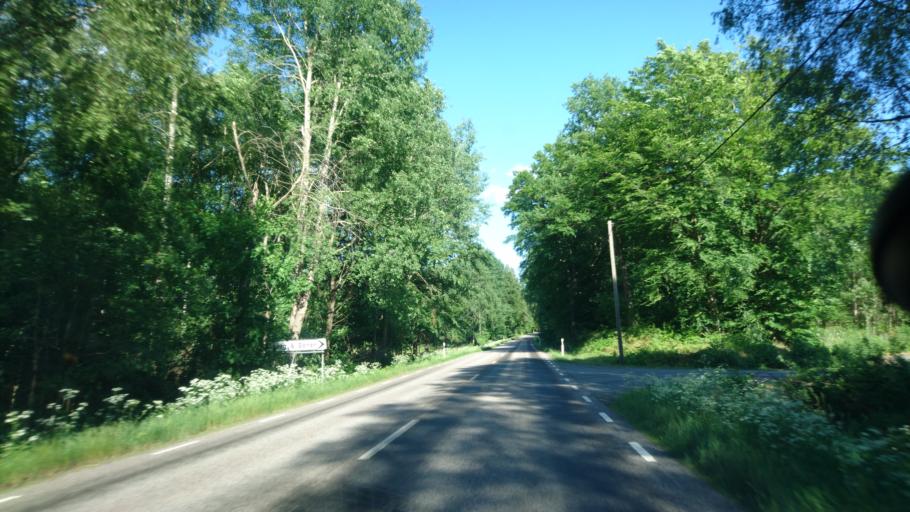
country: SE
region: Skane
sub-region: Osby Kommun
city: Lonsboda
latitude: 56.3908
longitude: 14.3564
